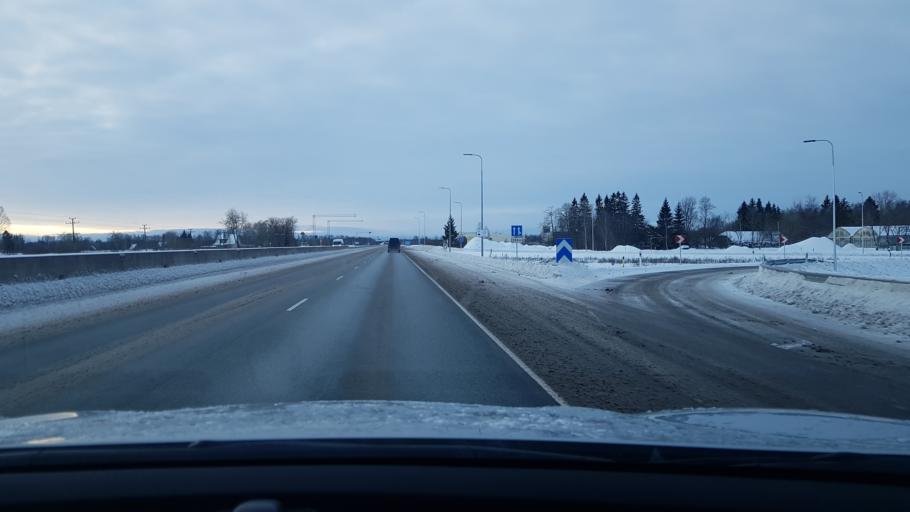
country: EE
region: Harju
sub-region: Joelaehtme vald
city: Loo
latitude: 59.4190
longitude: 24.9203
